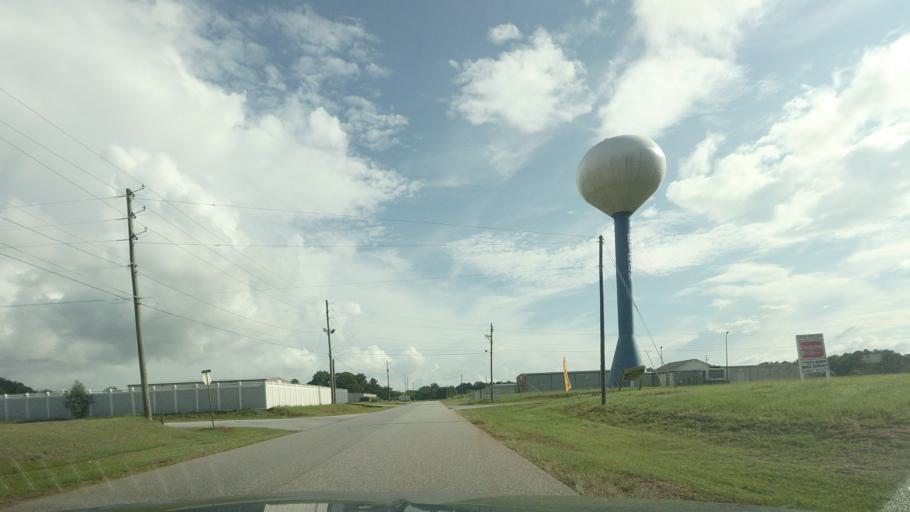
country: US
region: Georgia
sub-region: Peach County
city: Byron
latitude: 32.6474
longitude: -83.7407
